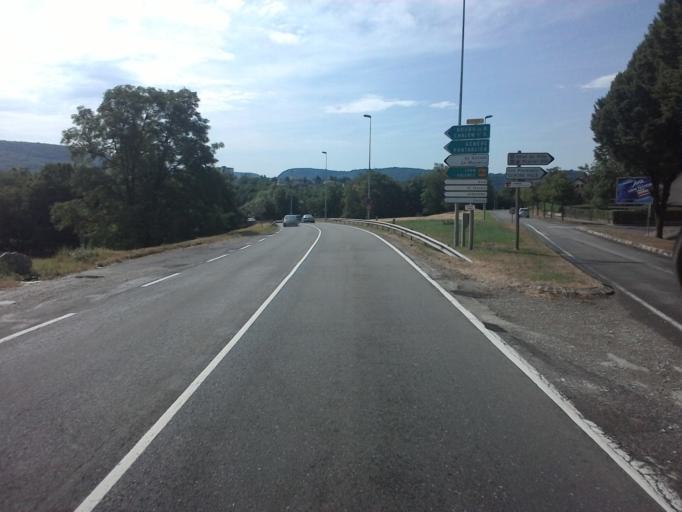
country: FR
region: Franche-Comte
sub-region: Departement du Jura
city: Lons-le-Saunier
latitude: 46.6887
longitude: 5.5619
